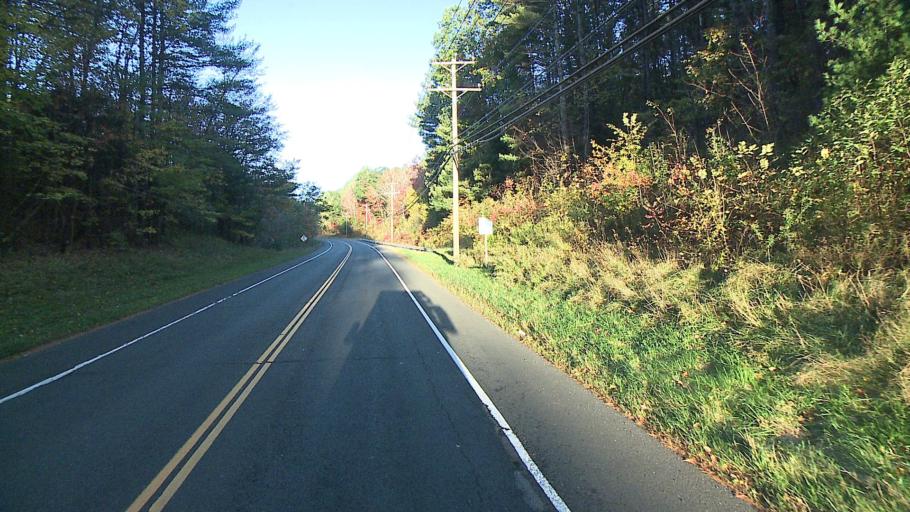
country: US
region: Connecticut
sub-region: Litchfield County
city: New Hartford Center
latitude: 41.9121
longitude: -73.0107
